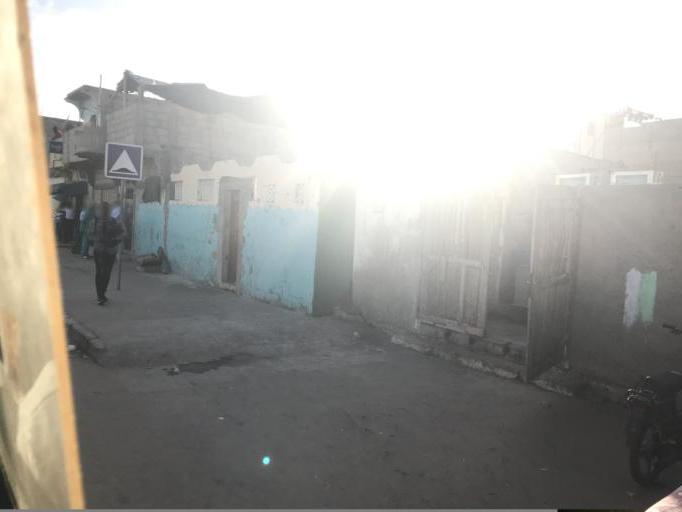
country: SN
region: Saint-Louis
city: Saint-Louis
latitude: 16.0222
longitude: -16.5077
